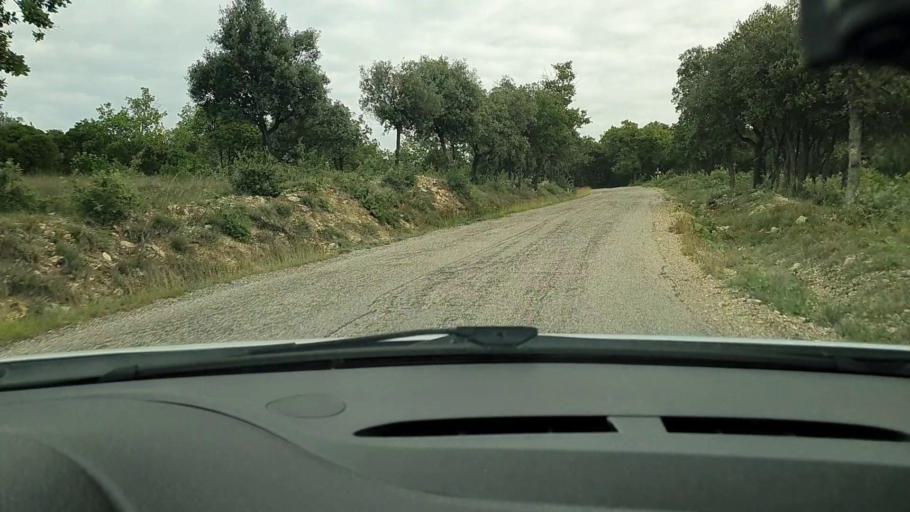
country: FR
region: Languedoc-Roussillon
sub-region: Departement du Gard
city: Montaren-et-Saint-Mediers
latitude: 44.0967
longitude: 4.2943
